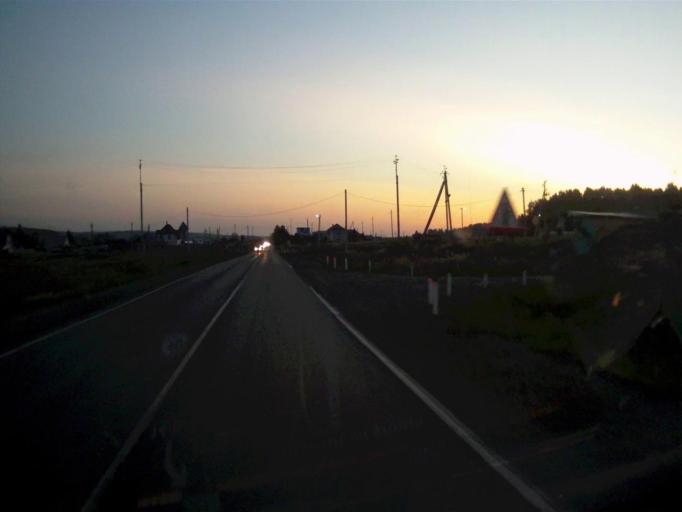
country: RU
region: Chelyabinsk
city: Poletayevo
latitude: 55.2246
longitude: 60.9943
